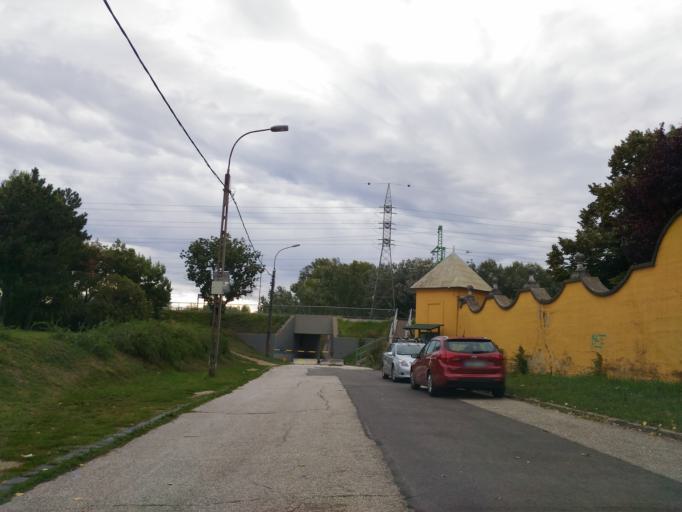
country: HU
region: Pest
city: Halasztelek
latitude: 47.3909
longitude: 18.9885
